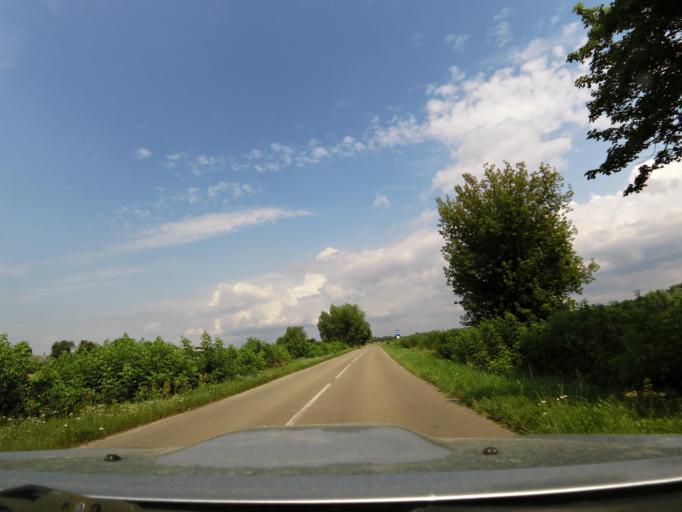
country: LT
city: Rusne
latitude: 55.3121
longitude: 21.3808
